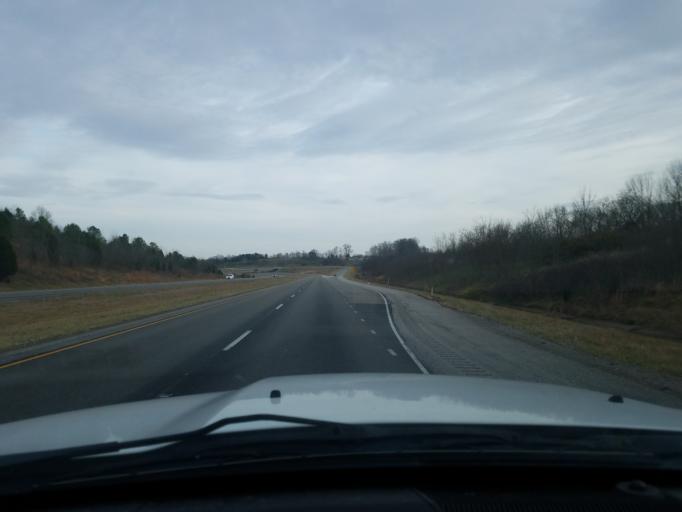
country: US
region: Indiana
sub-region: Crawford County
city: English
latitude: 38.2278
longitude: -86.5999
